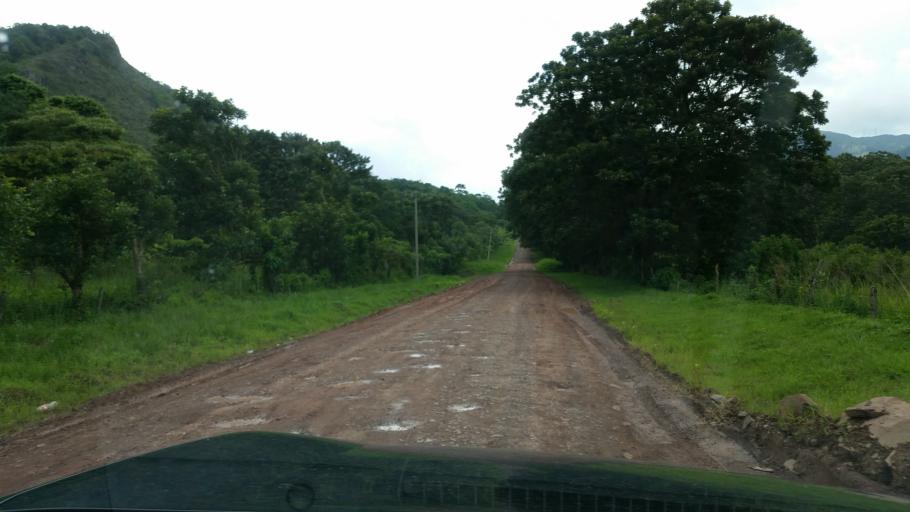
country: NI
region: Jinotega
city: Jinotega
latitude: 13.2215
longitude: -85.7309
